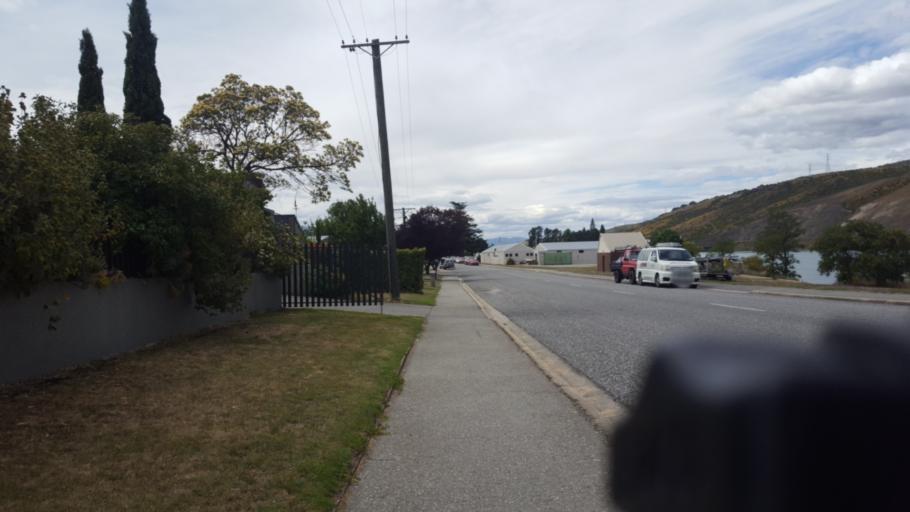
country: NZ
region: Otago
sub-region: Queenstown-Lakes District
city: Wanaka
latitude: -45.0477
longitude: 169.2118
